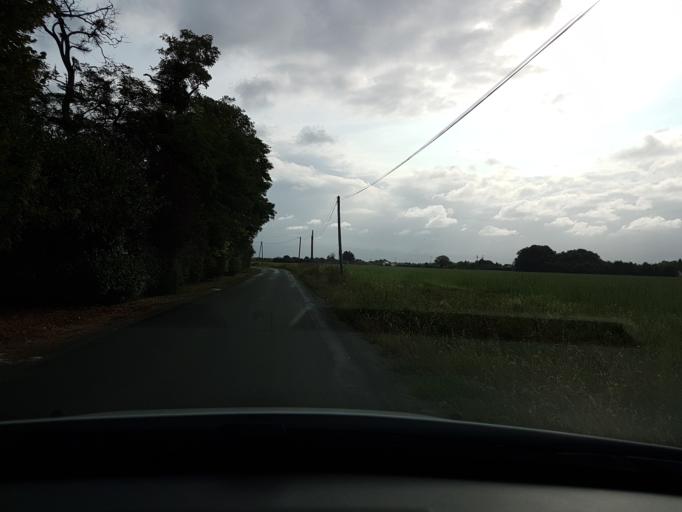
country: FR
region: Centre
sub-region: Departement d'Indre-et-Loire
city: Azay-sur-Cher
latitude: 47.3364
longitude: 0.8239
